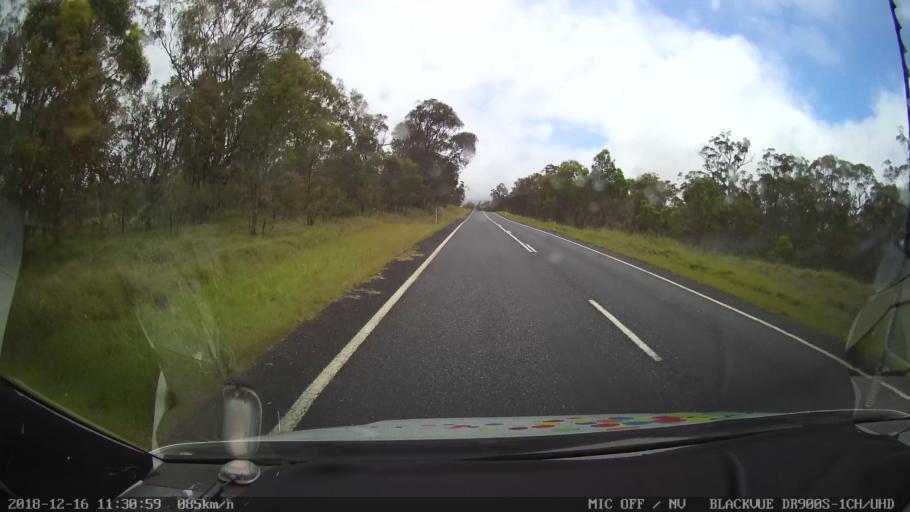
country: AU
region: New South Wales
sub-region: Tenterfield Municipality
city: Carrolls Creek
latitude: -29.0260
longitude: 152.1233
